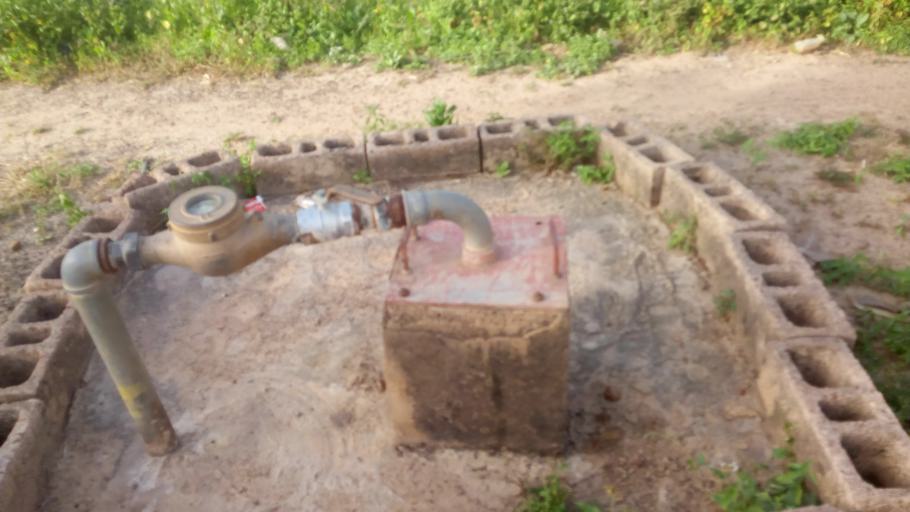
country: ML
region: Kayes
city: Kita
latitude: 13.1305
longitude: -8.8315
